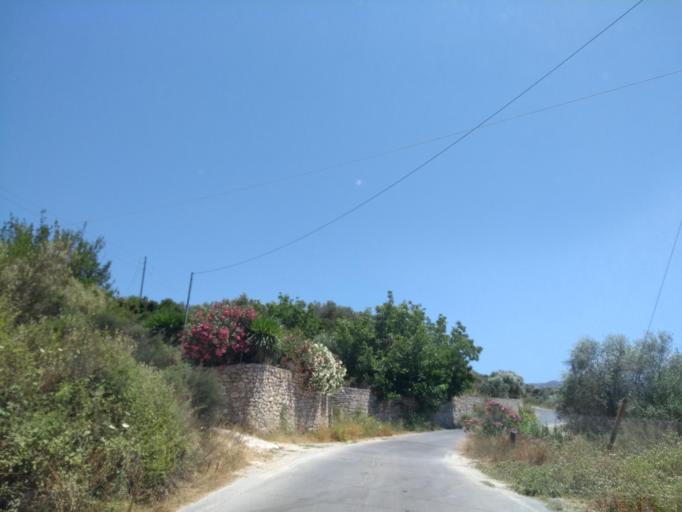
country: GR
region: Crete
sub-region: Nomos Chanias
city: Georgioupolis
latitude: 35.3290
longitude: 24.3227
